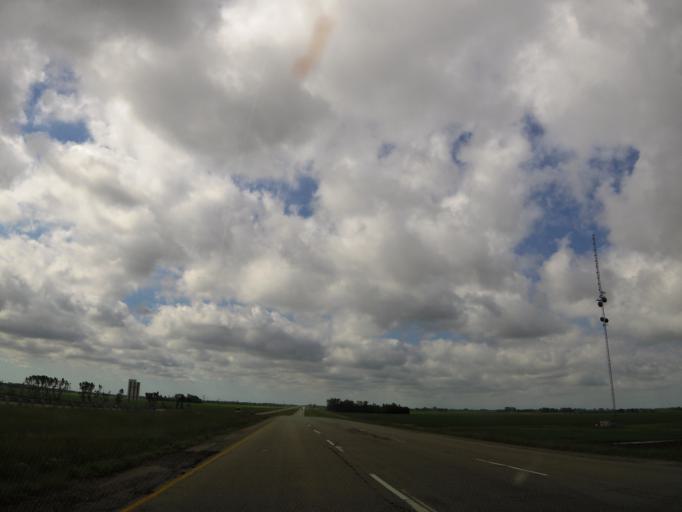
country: US
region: North Dakota
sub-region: Walsh County
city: Grafton
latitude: 48.1966
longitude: -97.1892
